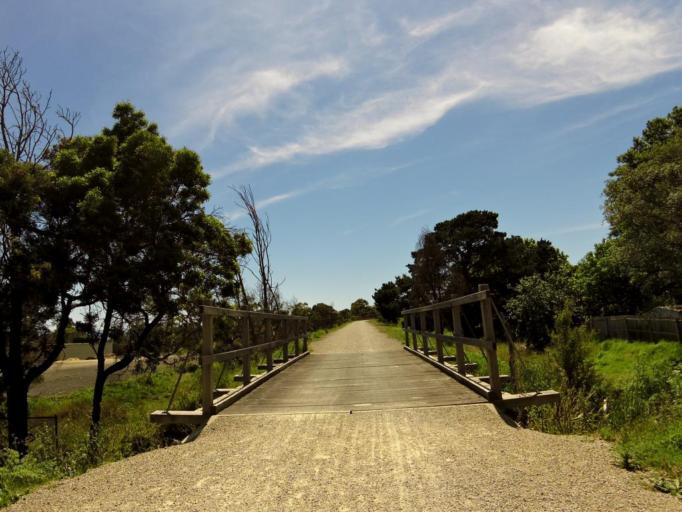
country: AU
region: Victoria
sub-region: Yarra Ranges
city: Lilydale
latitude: -37.7497
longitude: 145.3547
